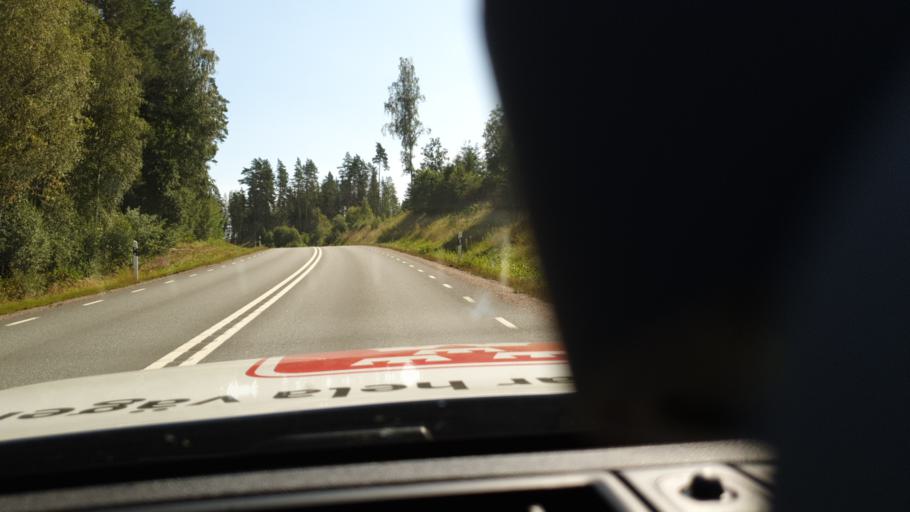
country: SE
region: Kalmar
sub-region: Hultsfreds Kommun
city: Virserum
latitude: 57.3955
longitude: 15.4808
